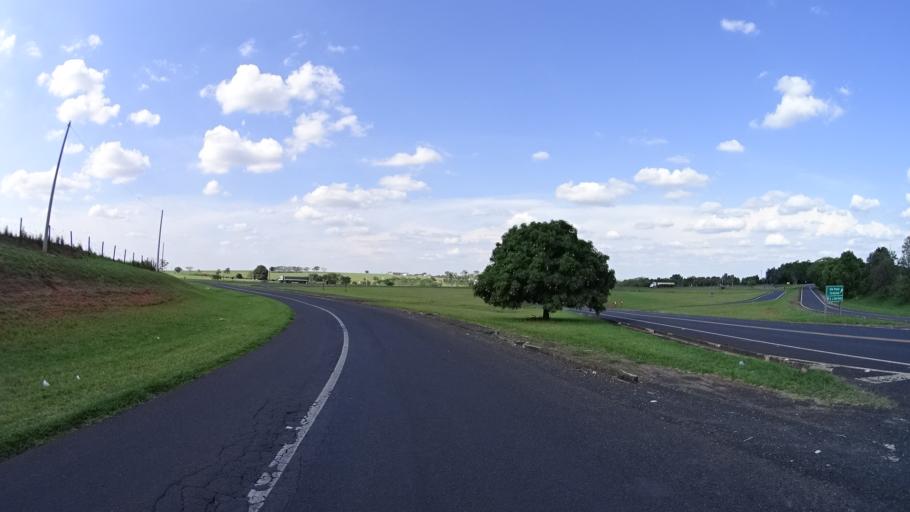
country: BR
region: Sao Paulo
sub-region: Guapiacu
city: Guapiacu
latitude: -20.9919
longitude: -49.2068
